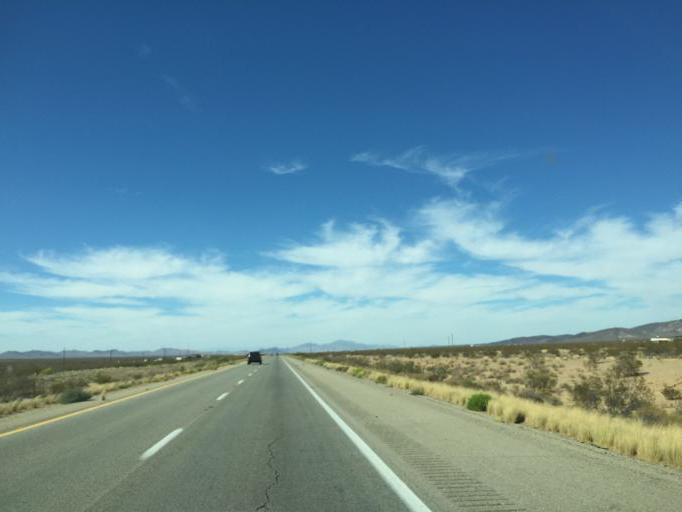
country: US
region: Arizona
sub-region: Mohave County
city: Dolan Springs
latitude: 35.5857
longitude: -114.3910
